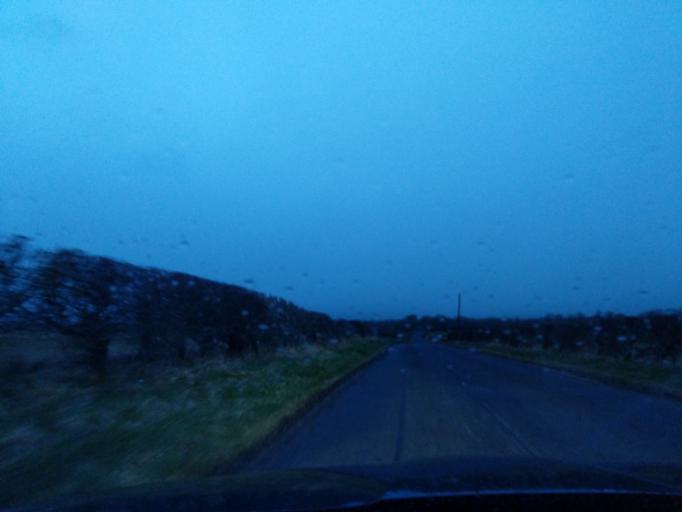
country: GB
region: England
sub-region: Northumberland
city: Ford
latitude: 55.7144
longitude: -2.1279
